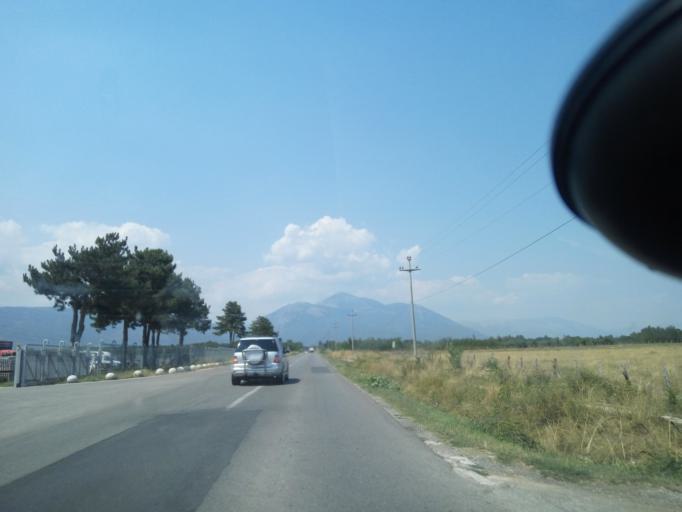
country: XK
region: Gjakova
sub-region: Komuna e Decanit
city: Prilep
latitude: 42.4795
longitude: 20.3345
